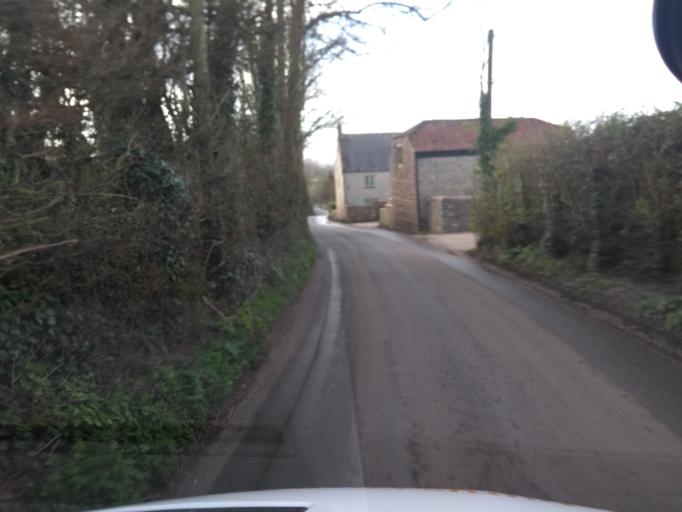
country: GB
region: England
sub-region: Somerset
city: Street
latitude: 51.1264
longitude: -2.8239
